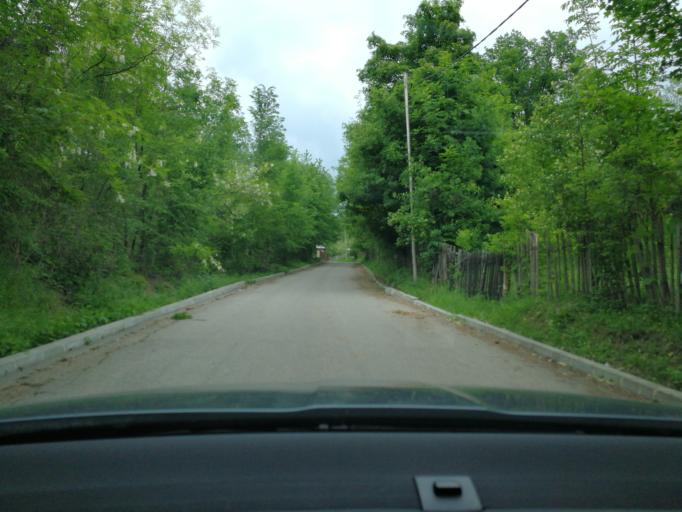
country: RO
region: Prahova
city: Cornu de Sus
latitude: 45.1664
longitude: 25.7054
